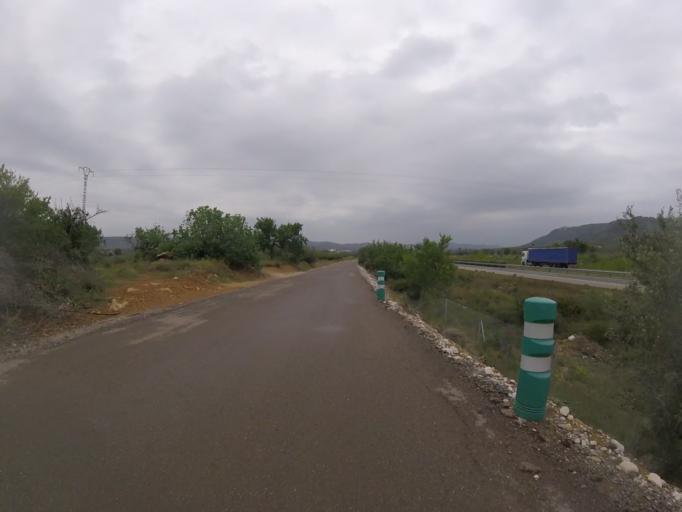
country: ES
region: Valencia
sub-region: Provincia de Castello
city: Alcala de Xivert
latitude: 40.2867
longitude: 0.2279
